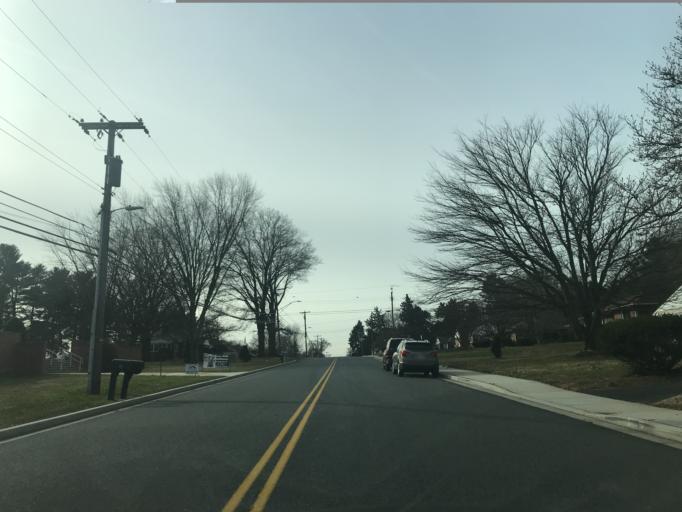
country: US
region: Maryland
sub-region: Harford County
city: Aberdeen
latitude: 39.5183
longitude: -76.1652
